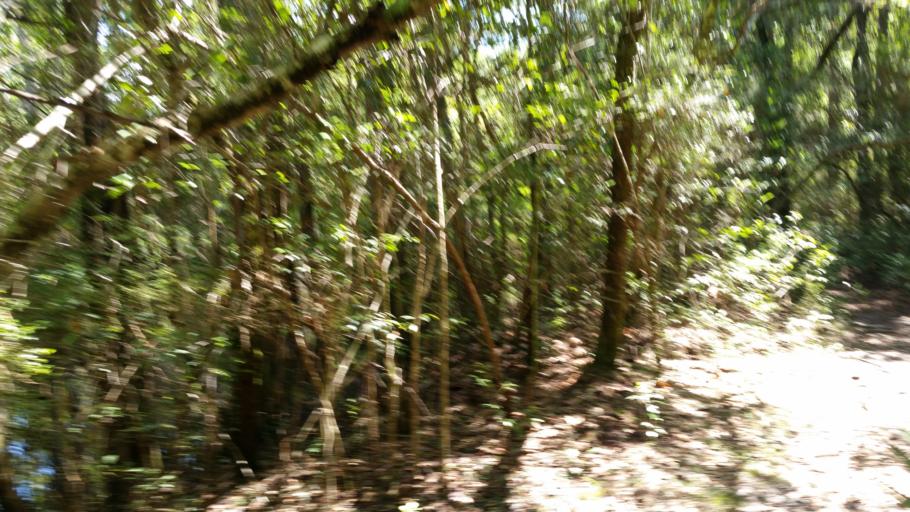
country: US
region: Florida
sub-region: Santa Rosa County
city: East Milton
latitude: 30.7061
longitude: -86.8749
